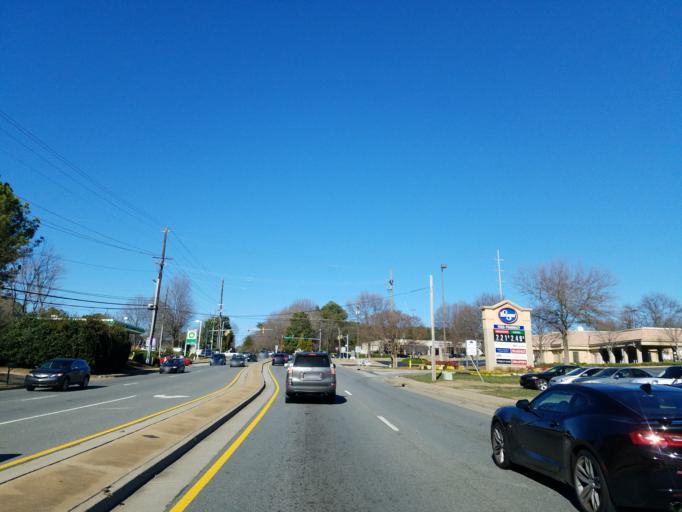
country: US
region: Georgia
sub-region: Fulton County
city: Roswell
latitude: 34.0259
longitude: -84.4242
